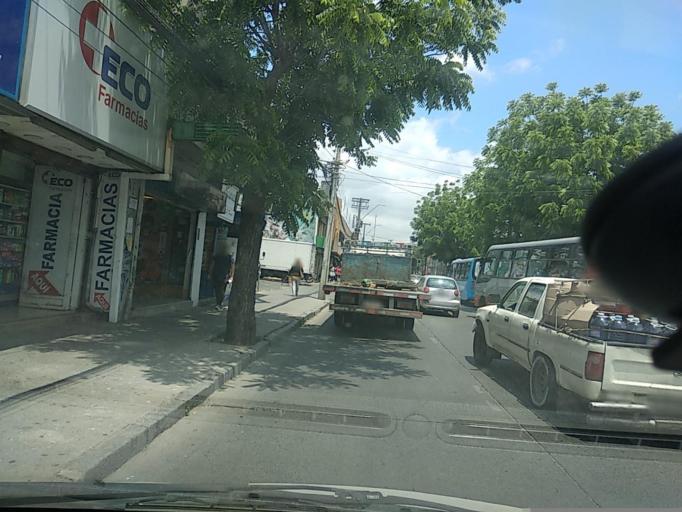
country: CL
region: Valparaiso
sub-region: Provincia de Marga Marga
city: Quilpue
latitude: -33.0474
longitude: -71.4422
